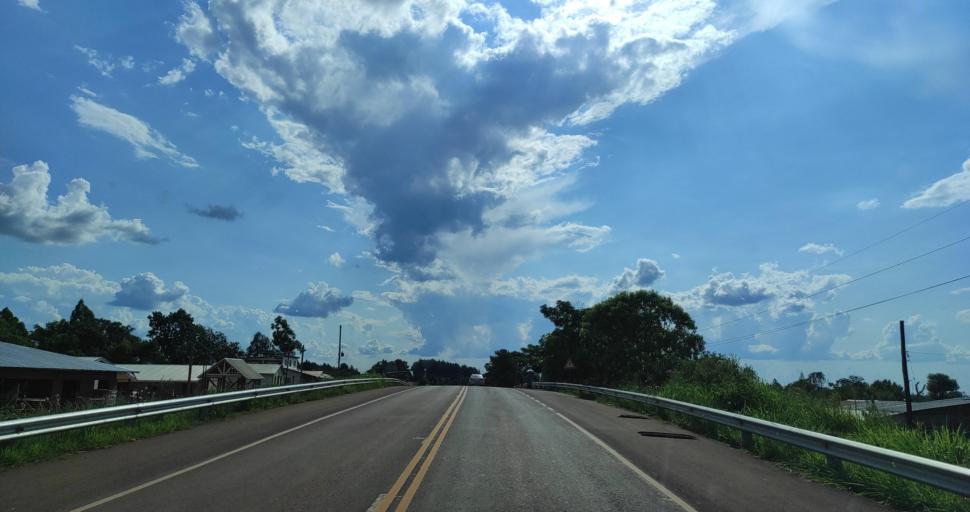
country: AR
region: Misiones
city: Bernardo de Irigoyen
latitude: -26.2956
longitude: -53.7891
